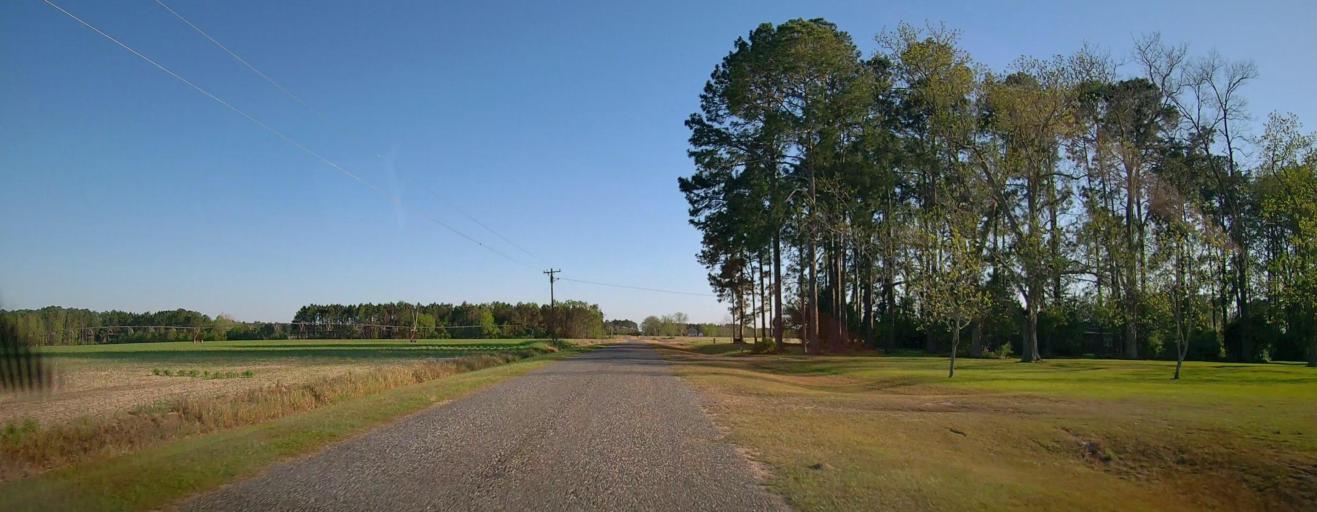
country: US
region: Georgia
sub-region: Ben Hill County
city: Fitzgerald
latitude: 31.6694
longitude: -83.1468
